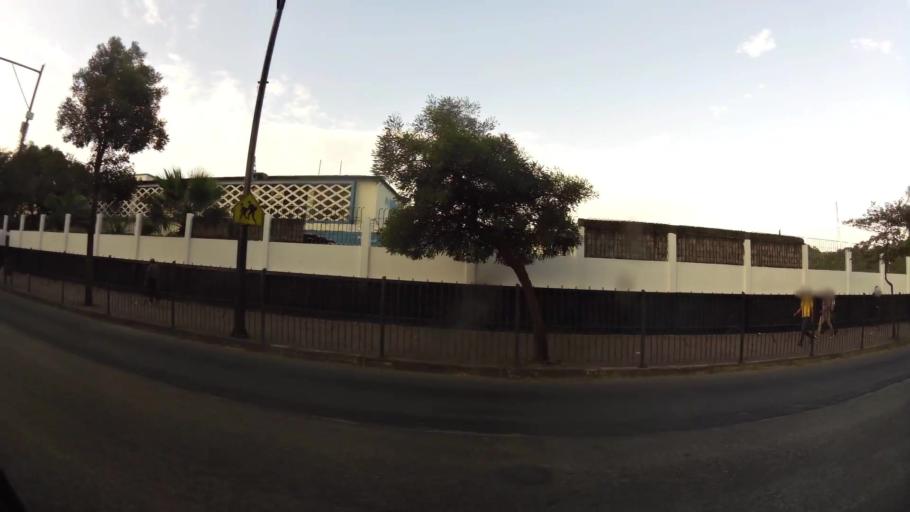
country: EC
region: Guayas
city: Guayaquil
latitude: -2.1779
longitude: -79.8910
